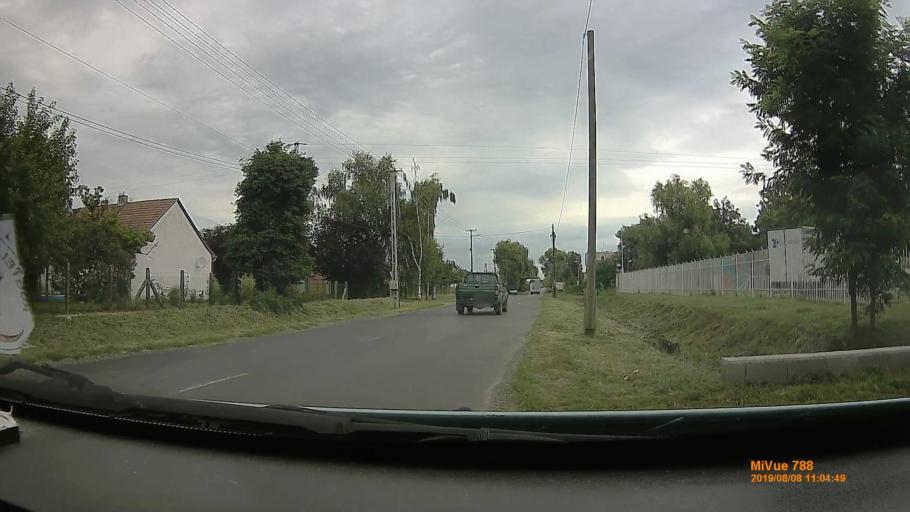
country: HU
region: Szabolcs-Szatmar-Bereg
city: Balkany
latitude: 47.7699
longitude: 21.8376
